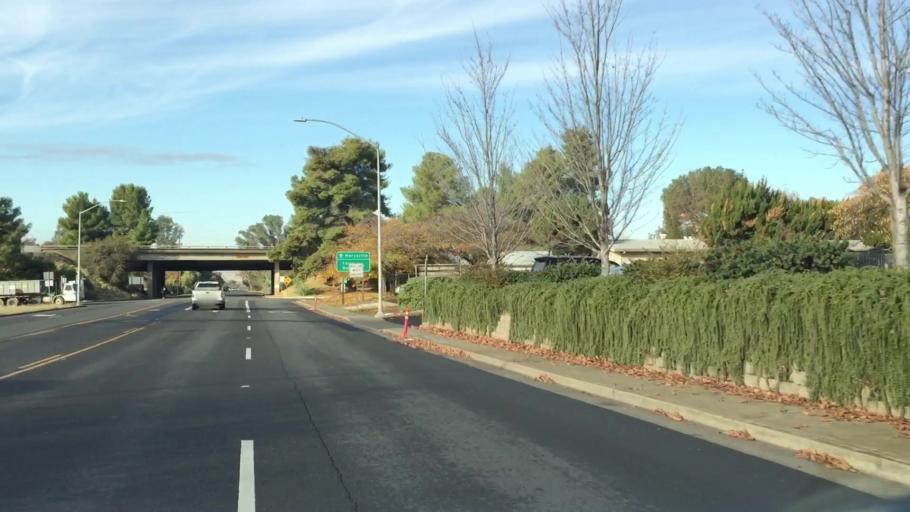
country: US
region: California
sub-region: Butte County
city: Oroville
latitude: 39.5242
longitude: -121.5714
